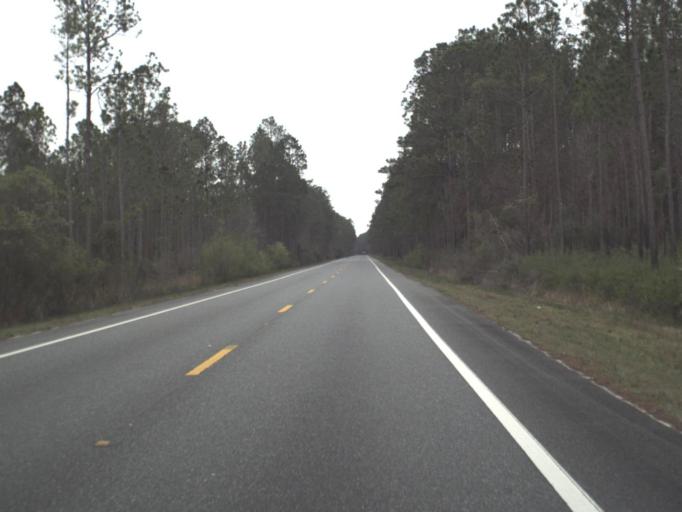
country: US
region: Florida
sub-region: Franklin County
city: Apalachicola
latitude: 29.9734
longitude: -84.9751
